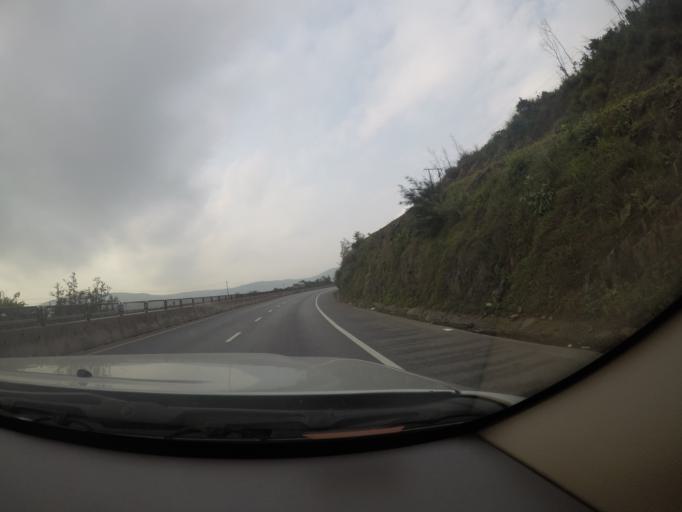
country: VN
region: Ha Tinh
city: Ky Anh
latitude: 17.9829
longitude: 106.4812
